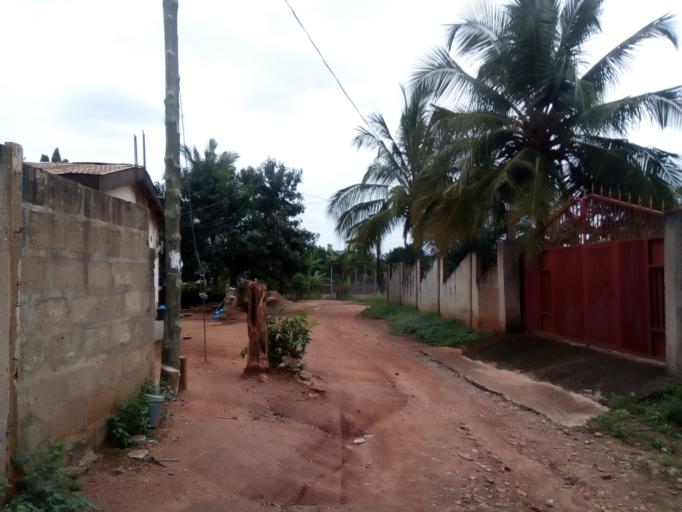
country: GH
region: Eastern
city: Nsawam
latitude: 5.7803
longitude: -0.3384
